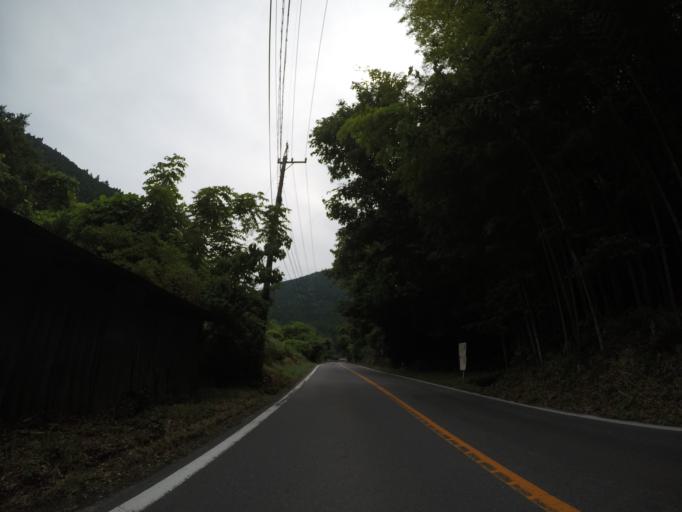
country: JP
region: Shizuoka
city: Fujinomiya
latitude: 35.2014
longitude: 138.5432
